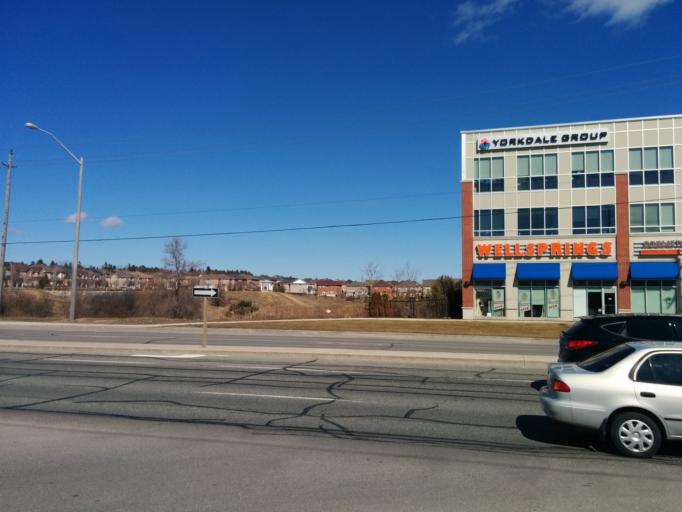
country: CA
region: Ontario
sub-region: York
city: Richmond Hill
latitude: 43.9129
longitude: -79.4472
